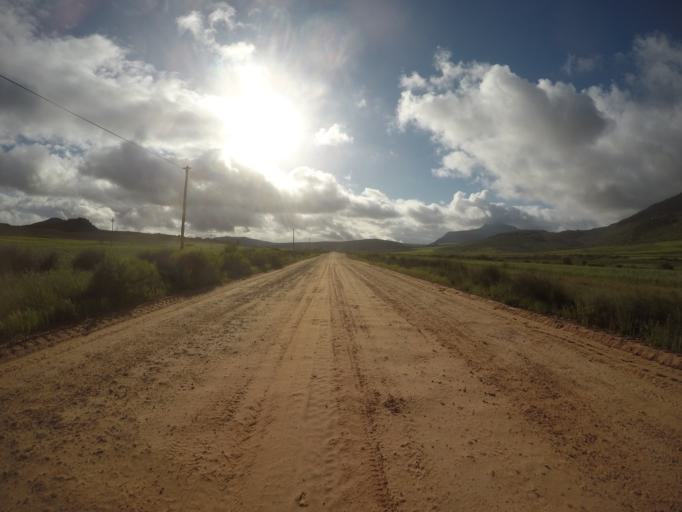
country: ZA
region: Western Cape
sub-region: West Coast District Municipality
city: Clanwilliam
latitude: -32.3432
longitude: 18.8252
